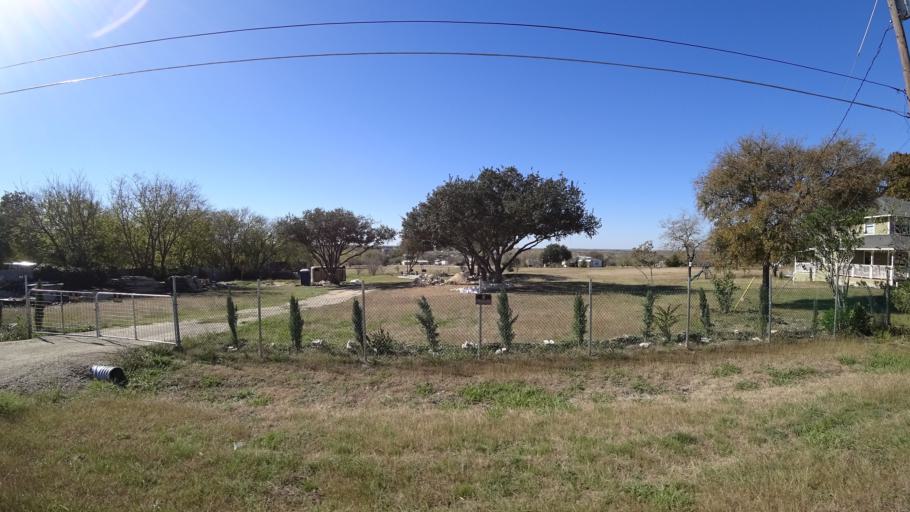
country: US
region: Texas
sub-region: Travis County
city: Garfield
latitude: 30.1046
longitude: -97.5944
